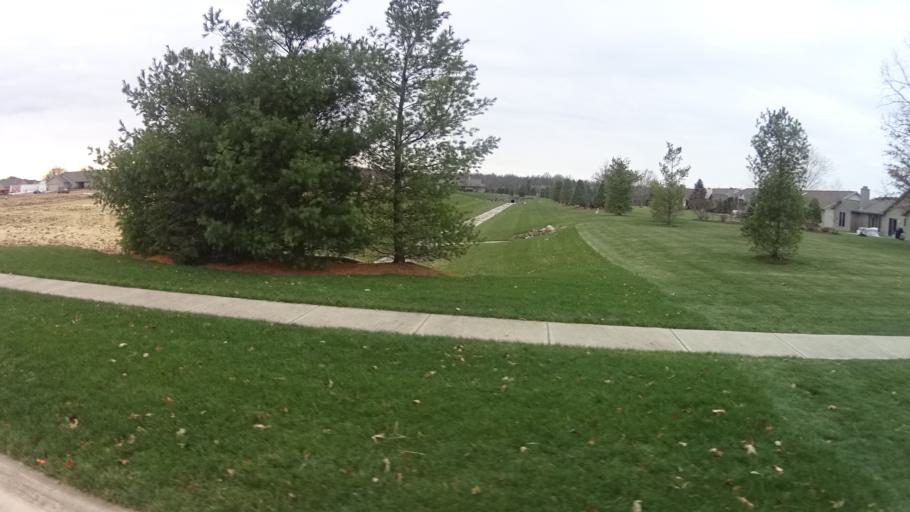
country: US
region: Ohio
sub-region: Lorain County
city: North Ridgeville
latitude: 41.3600
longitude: -81.9817
